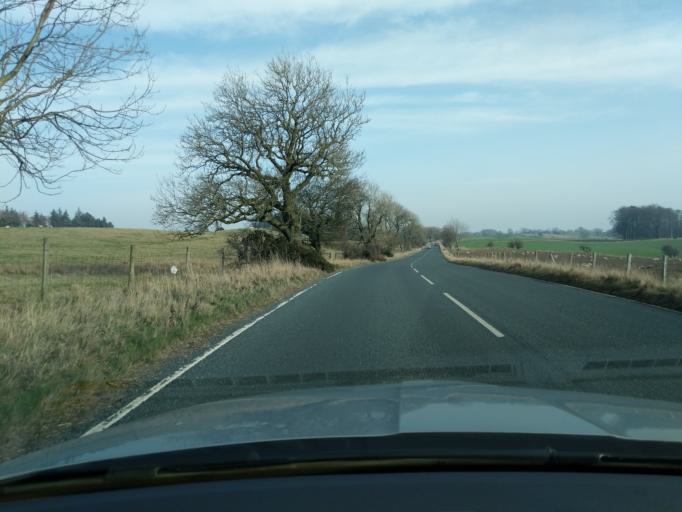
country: GB
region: England
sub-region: North Yorkshire
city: Catterick Garrison
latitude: 54.3474
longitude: -1.7660
